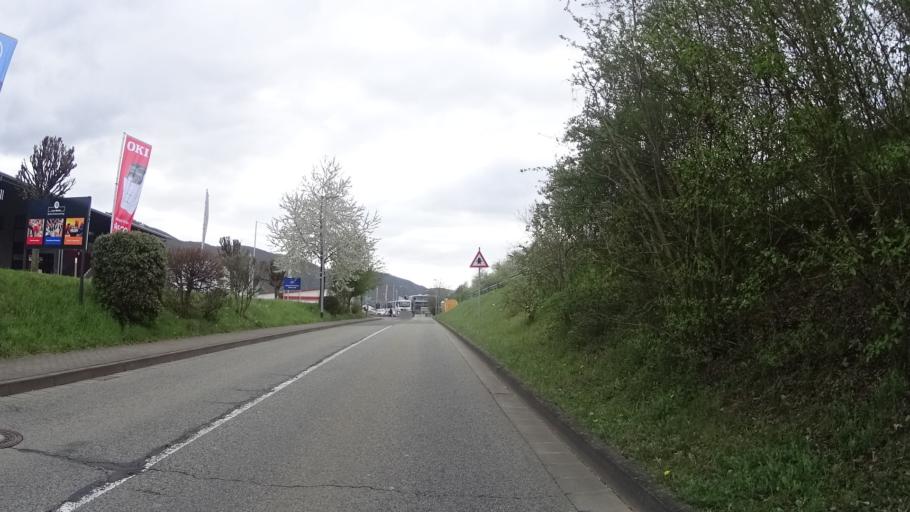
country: DE
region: Rheinland-Pfalz
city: Kamp-Bornhofen
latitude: 50.2116
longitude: 7.6225
